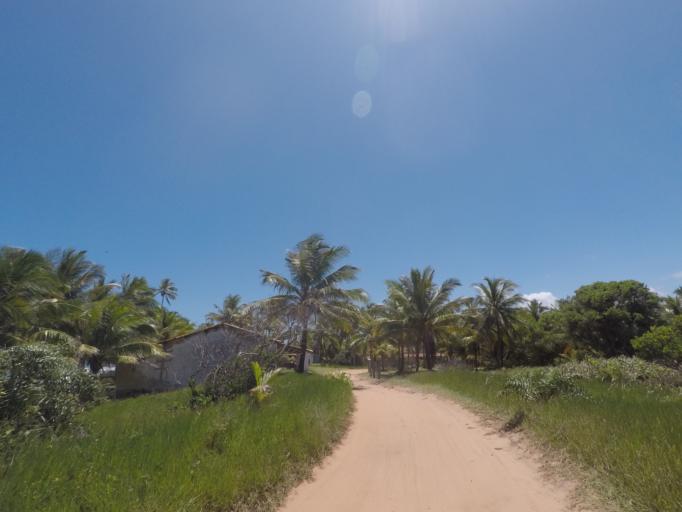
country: BR
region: Bahia
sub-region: Marau
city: Marau
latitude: -14.0206
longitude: -38.9462
